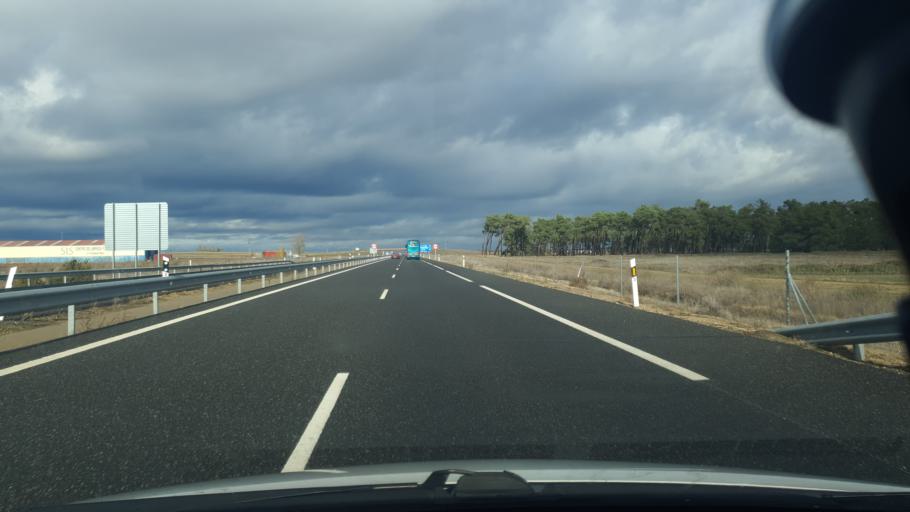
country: ES
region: Castille and Leon
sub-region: Provincia de Segovia
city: Navalmanzano
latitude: 41.1936
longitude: -4.2657
